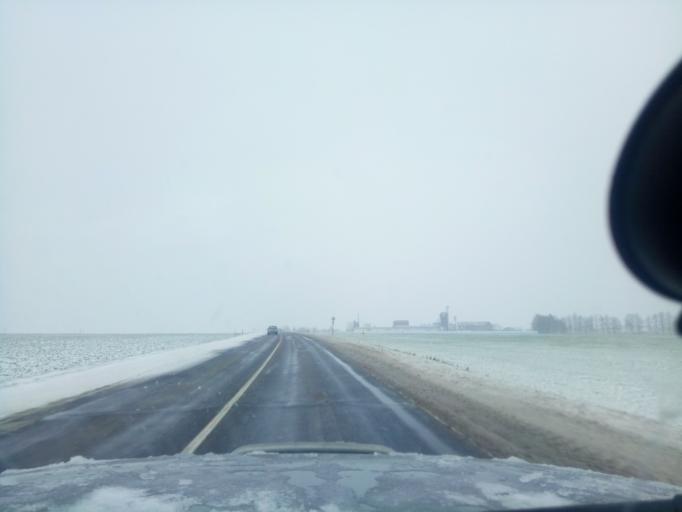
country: BY
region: Minsk
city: Haradzyeya
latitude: 53.3226
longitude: 26.5552
